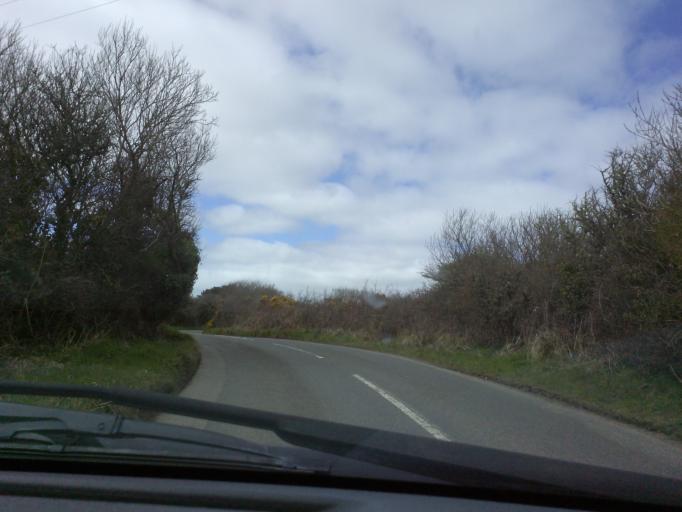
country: GB
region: England
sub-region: Cornwall
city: St. Buryan
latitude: 50.0591
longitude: -5.6252
